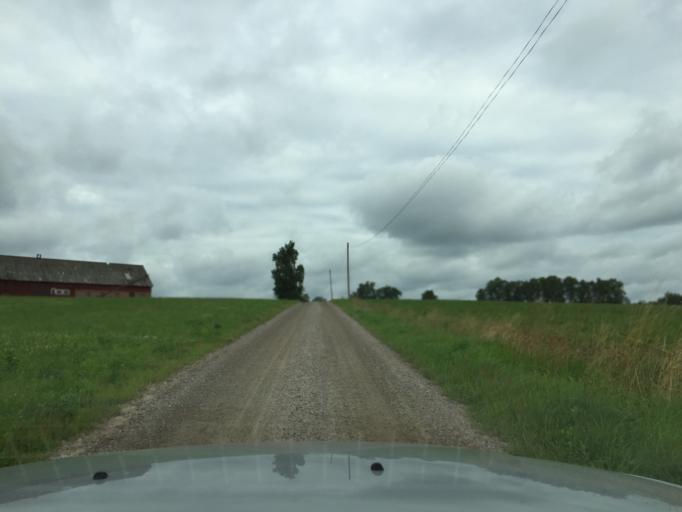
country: SE
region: Skane
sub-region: Hassleholms Kommun
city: Sosdala
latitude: 56.0307
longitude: 13.6583
